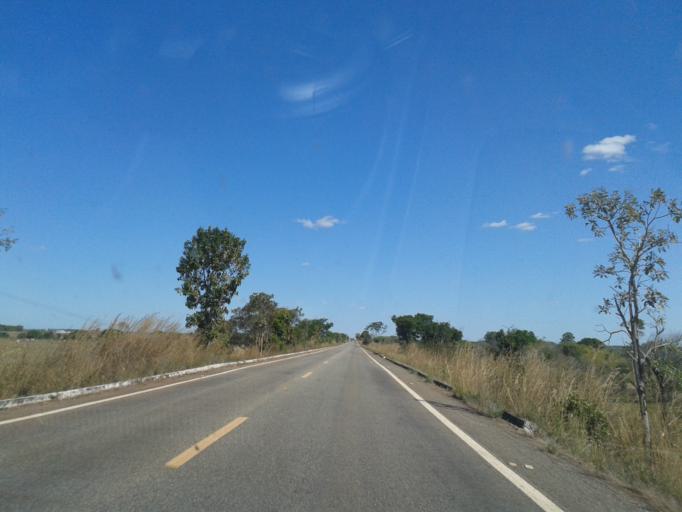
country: BR
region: Goias
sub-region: Sao Miguel Do Araguaia
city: Sao Miguel do Araguaia
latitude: -13.5899
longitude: -50.3172
